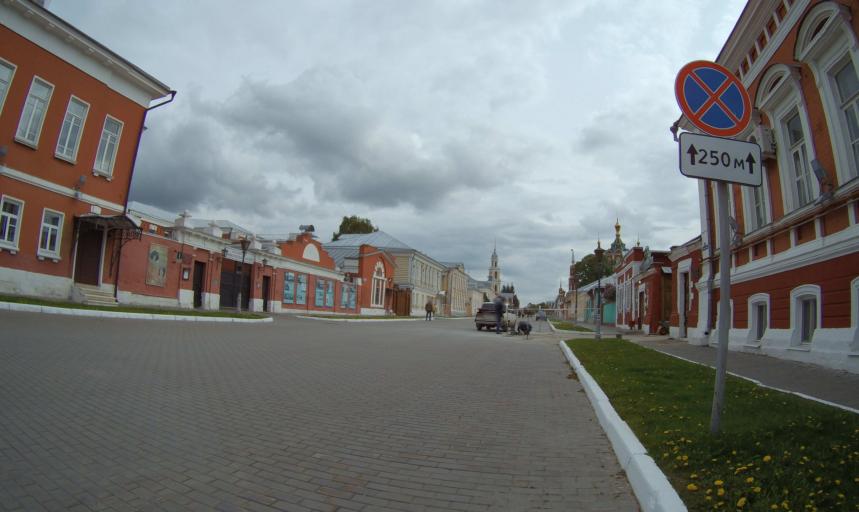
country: RU
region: Moskovskaya
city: Kolomna
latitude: 55.1057
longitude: 38.7526
